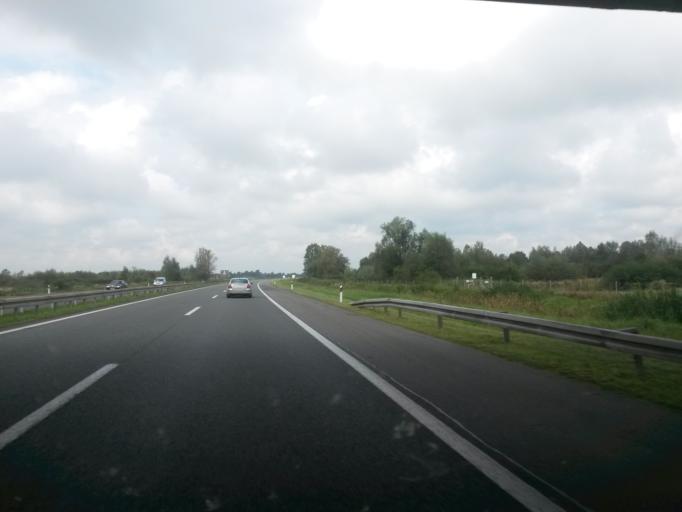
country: HR
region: Zagrebacka
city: Lupoglav
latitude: 45.6930
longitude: 16.3701
